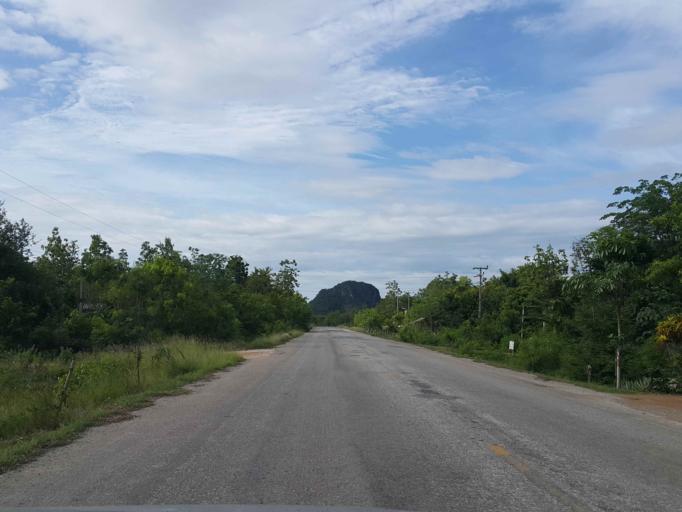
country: TH
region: Sukhothai
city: Thung Saliam
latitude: 17.2991
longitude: 99.5271
